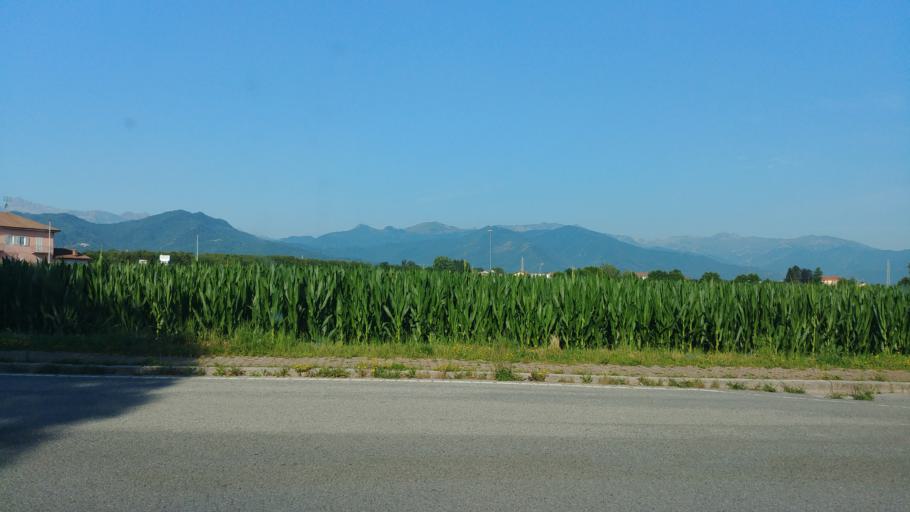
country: IT
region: Piedmont
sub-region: Provincia di Cuneo
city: San Defendente
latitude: 44.3954
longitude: 7.5174
